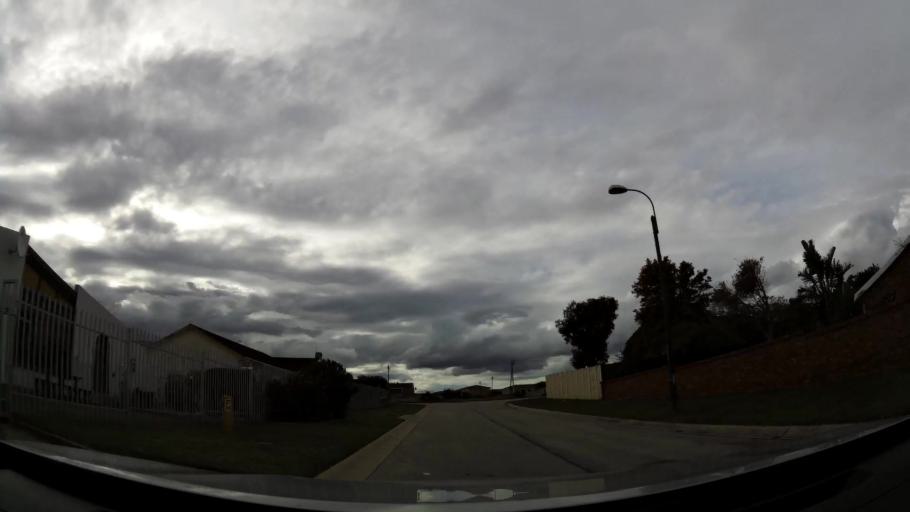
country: ZA
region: Eastern Cape
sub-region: Nelson Mandela Bay Metropolitan Municipality
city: Port Elizabeth
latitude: -33.9428
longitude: 25.4857
